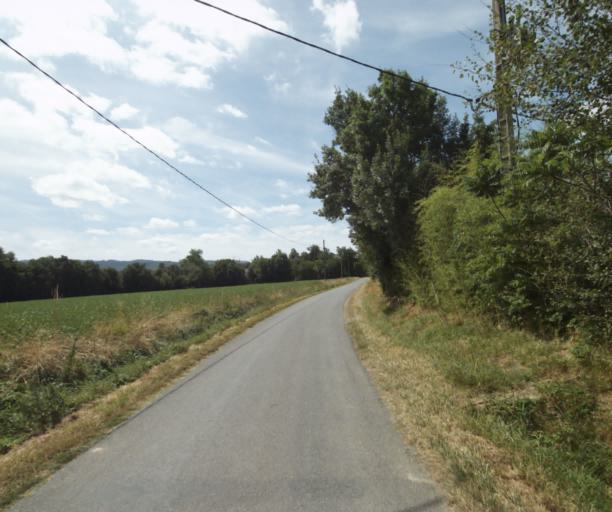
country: FR
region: Midi-Pyrenees
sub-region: Departement du Tarn
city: Soreze
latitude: 43.4961
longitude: 2.0829
